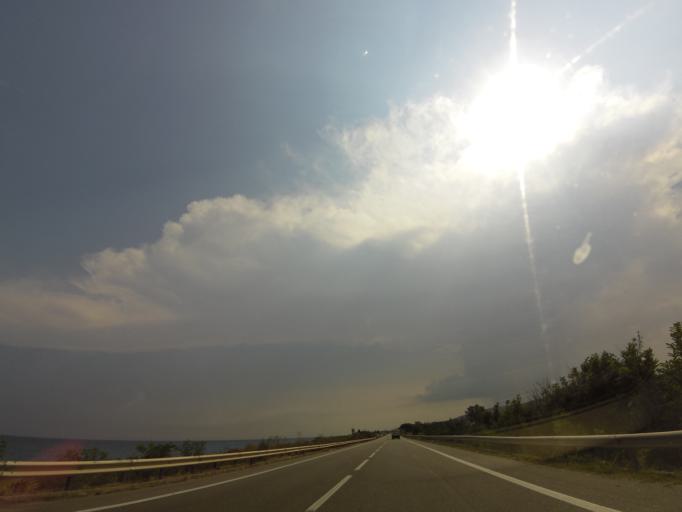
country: IT
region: Calabria
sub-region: Provincia di Reggio Calabria
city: Monasterace Marina
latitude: 38.4246
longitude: 16.5679
